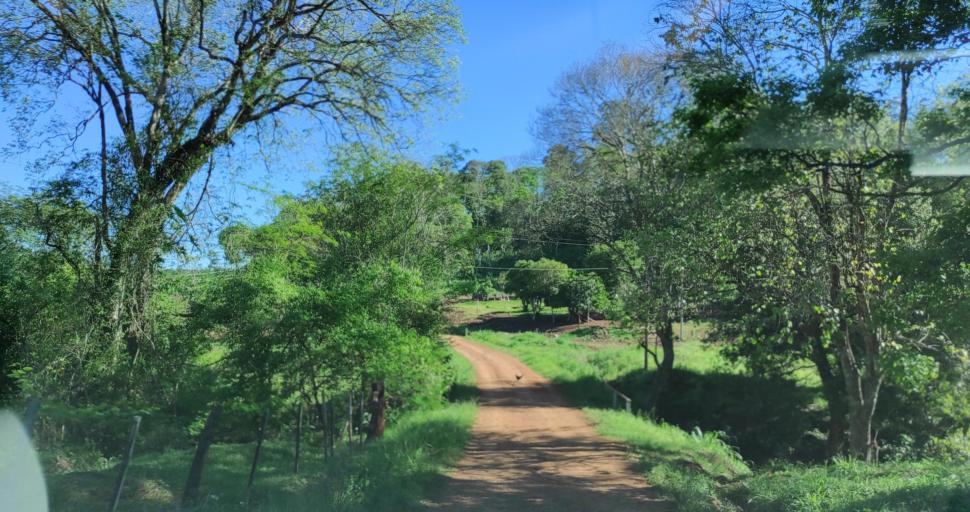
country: AR
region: Misiones
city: Capiovi
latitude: -26.9217
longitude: -55.0793
